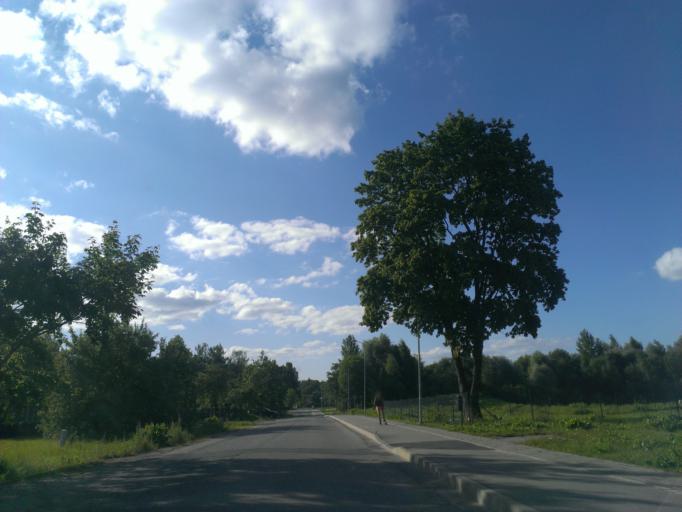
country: LV
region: Sigulda
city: Sigulda
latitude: 57.1661
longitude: 24.8735
